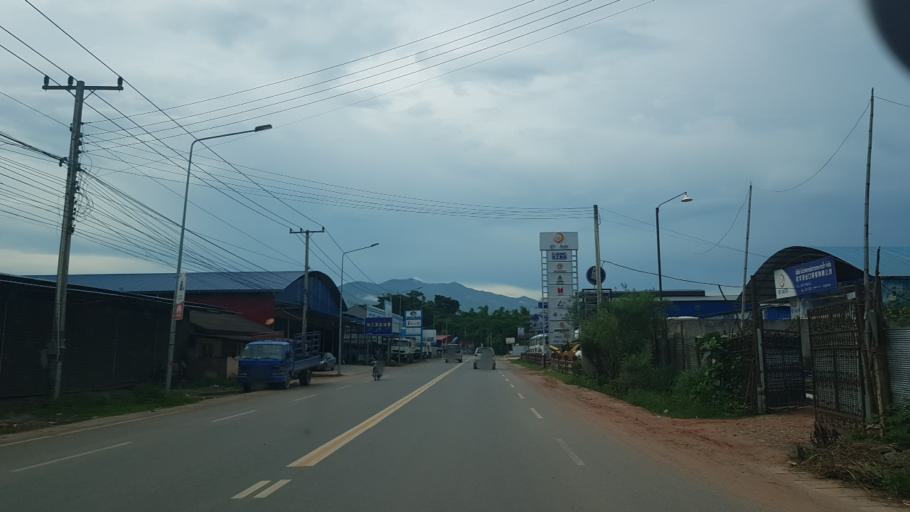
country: LA
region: Oudomxai
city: Muang Xay
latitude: 20.6691
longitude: 101.9827
